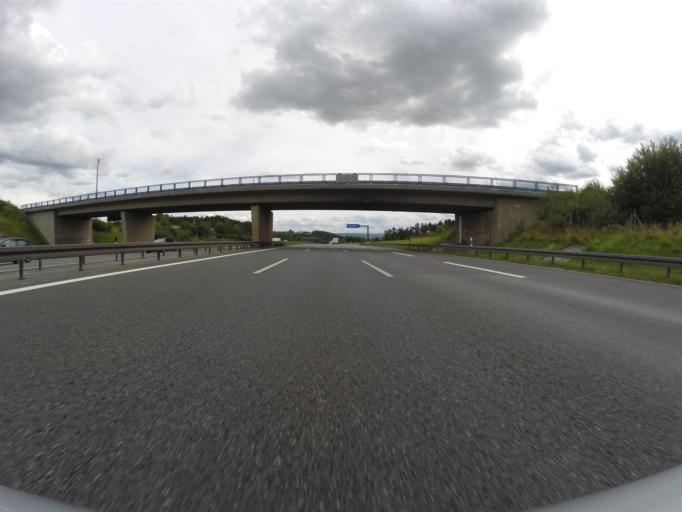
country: DE
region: Bavaria
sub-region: Upper Franconia
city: Bindlach
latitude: 50.0152
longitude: 11.6054
